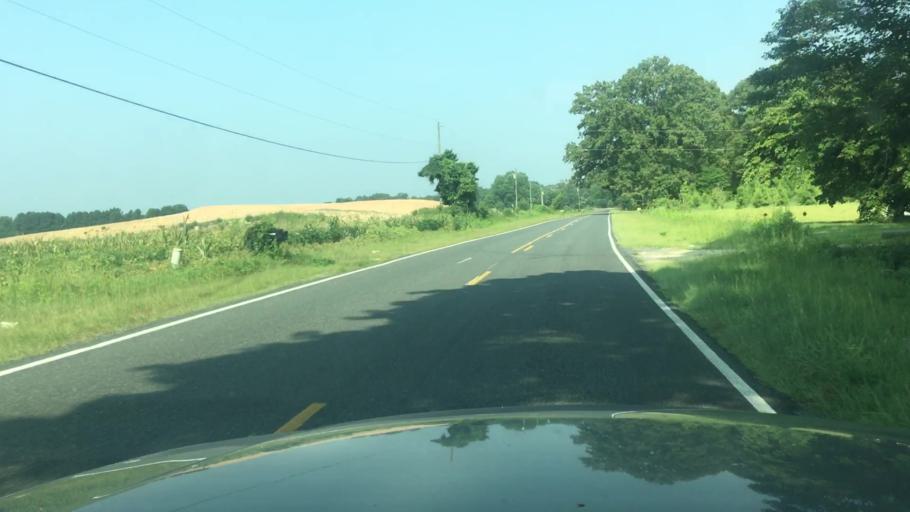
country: US
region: North Carolina
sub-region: Cumberland County
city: Hope Mills
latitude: 34.9091
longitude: -78.8624
